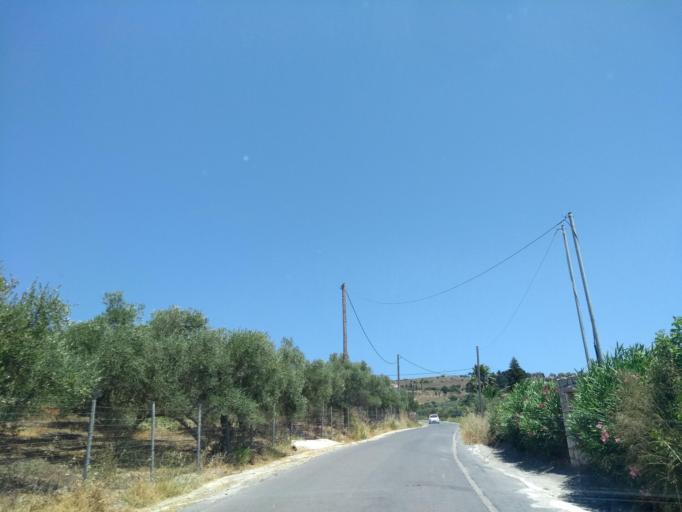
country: GR
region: Crete
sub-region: Nomos Chanias
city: Georgioupolis
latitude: 35.3251
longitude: 24.3268
